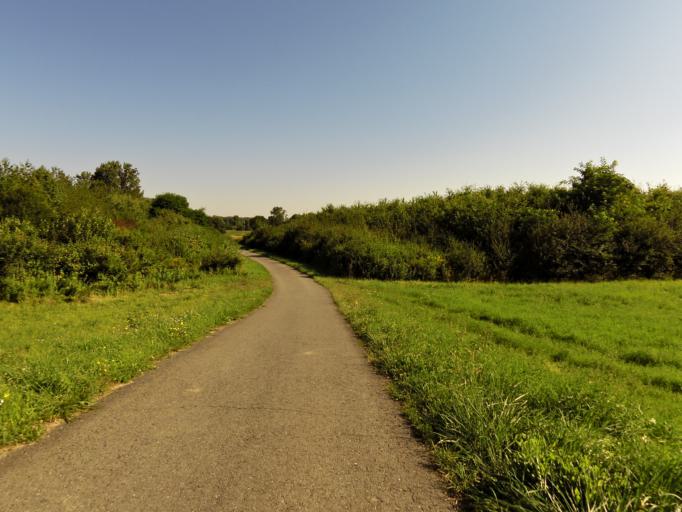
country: DE
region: Hesse
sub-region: Regierungsbezirk Darmstadt
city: Stockstadt am Rhein
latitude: 49.8015
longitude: 8.4541
